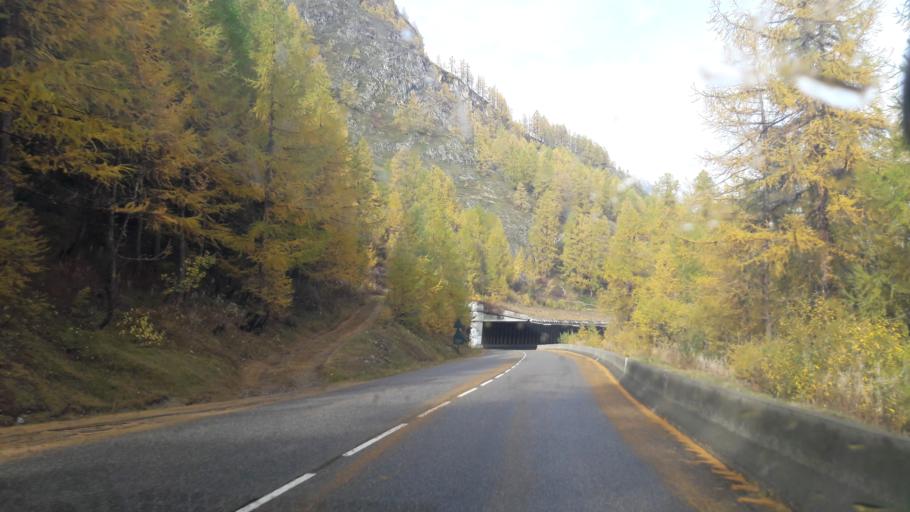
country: FR
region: Rhone-Alpes
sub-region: Departement de la Savoie
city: Tignes
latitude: 45.4869
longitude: 6.9279
